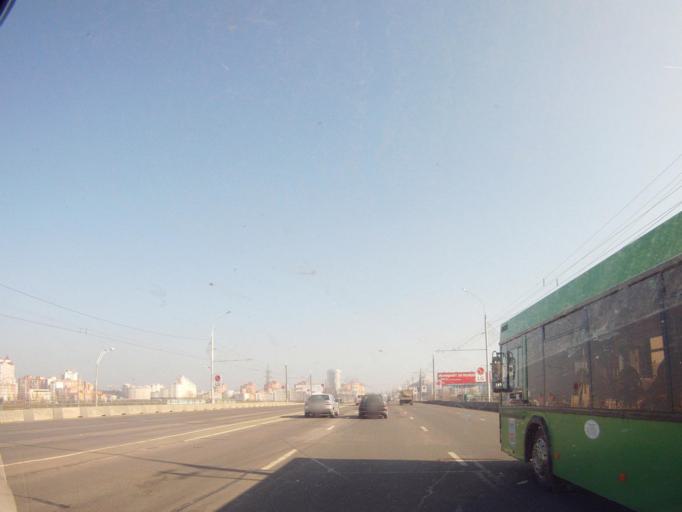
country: BY
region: Minsk
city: Borovlyany
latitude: 53.9405
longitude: 27.6721
